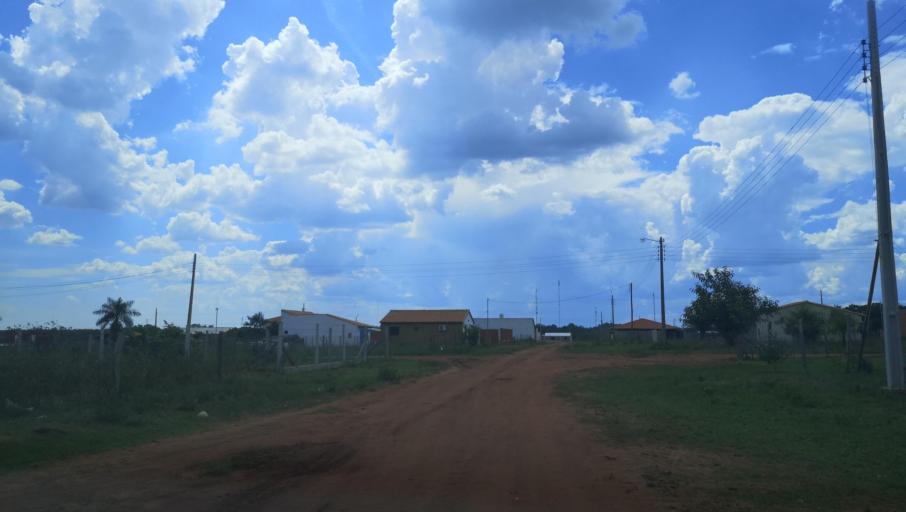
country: PY
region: Misiones
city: Santa Maria
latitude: -26.8977
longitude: -57.0407
